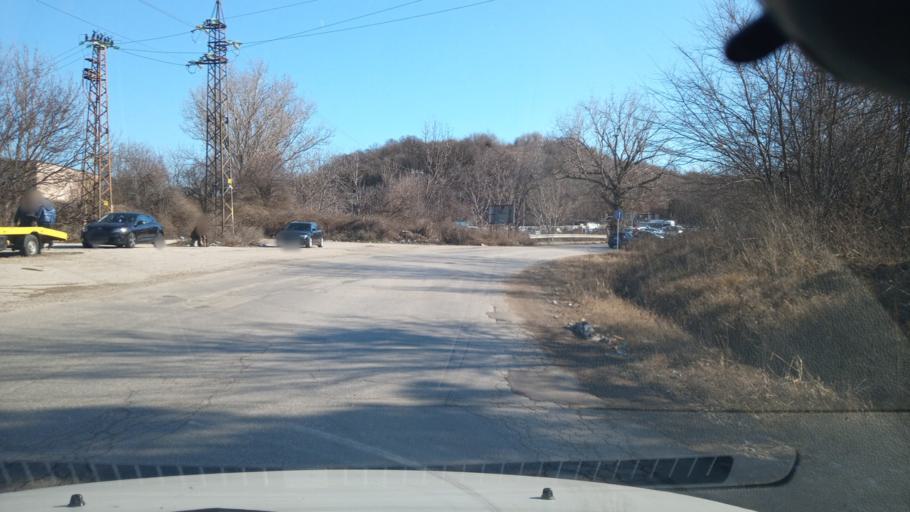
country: BG
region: Pleven
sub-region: Obshtina Pleven
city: Pleven
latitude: 43.4399
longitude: 24.5965
